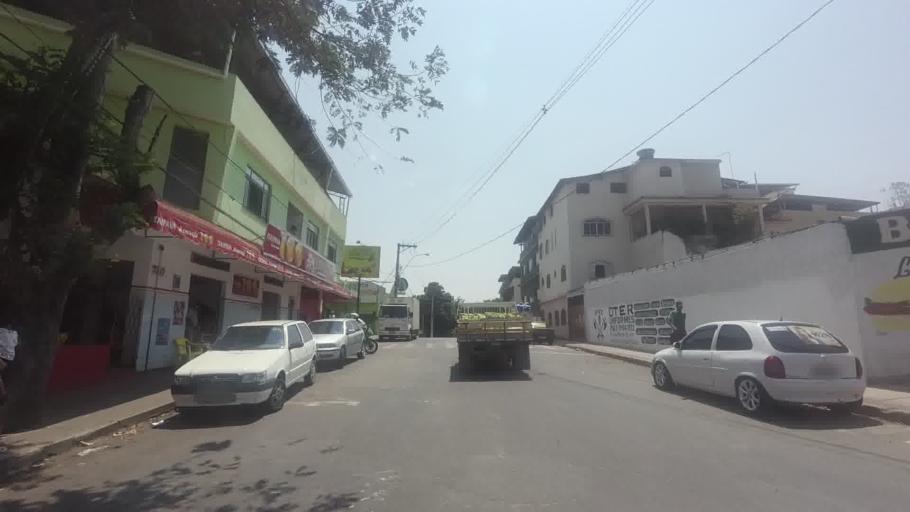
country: BR
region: Espirito Santo
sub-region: Cachoeiro De Itapemirim
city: Cachoeiro de Itapemirim
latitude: -20.8432
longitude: -41.1161
